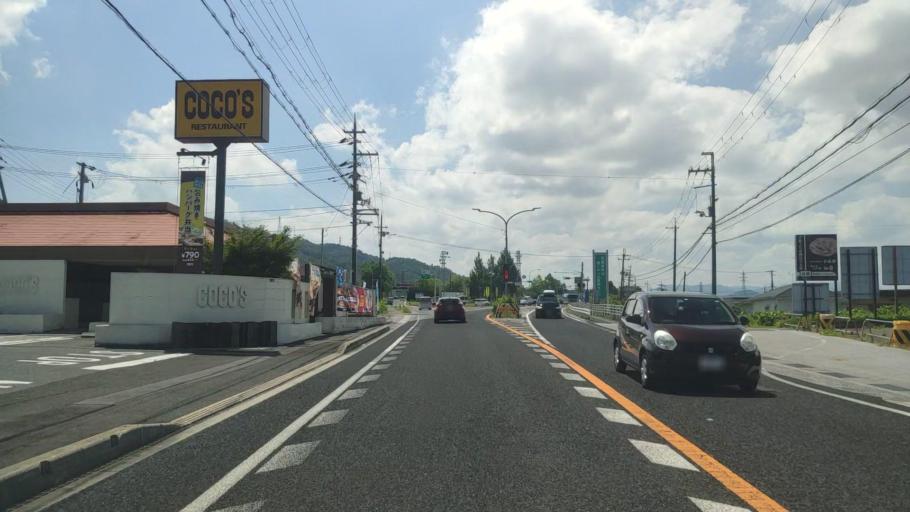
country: JP
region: Shiga Prefecture
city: Hikone
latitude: 35.2629
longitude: 136.2710
